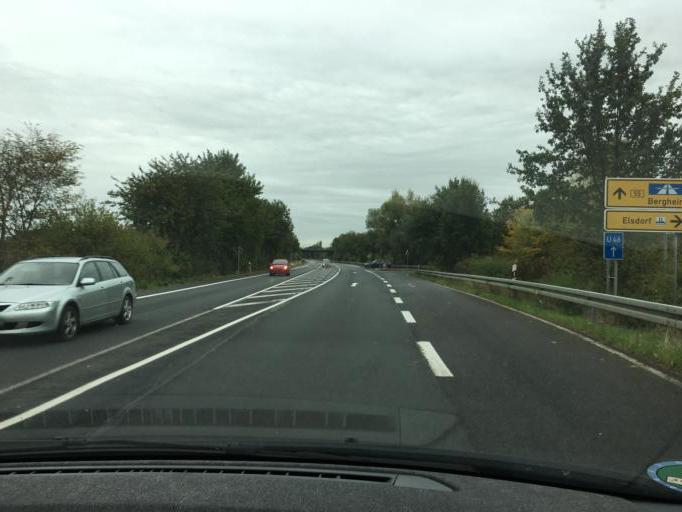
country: DE
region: North Rhine-Westphalia
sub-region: Regierungsbezirk Koln
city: Elsdorf
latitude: 50.9468
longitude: 6.5788
